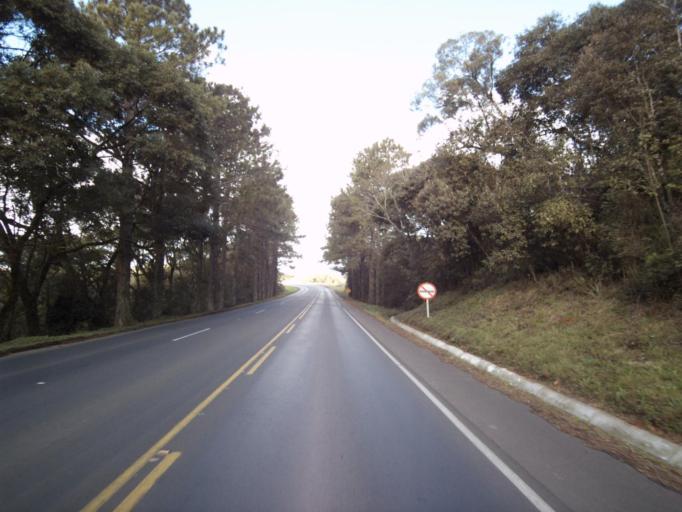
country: BR
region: Santa Catarina
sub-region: Concordia
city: Concordia
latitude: -26.9823
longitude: -51.7939
